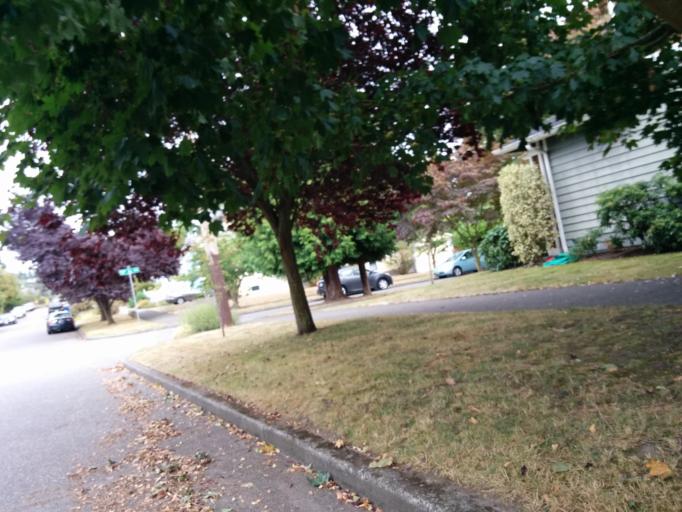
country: US
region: Washington
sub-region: King County
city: Seattle
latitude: 47.6724
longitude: -122.3711
